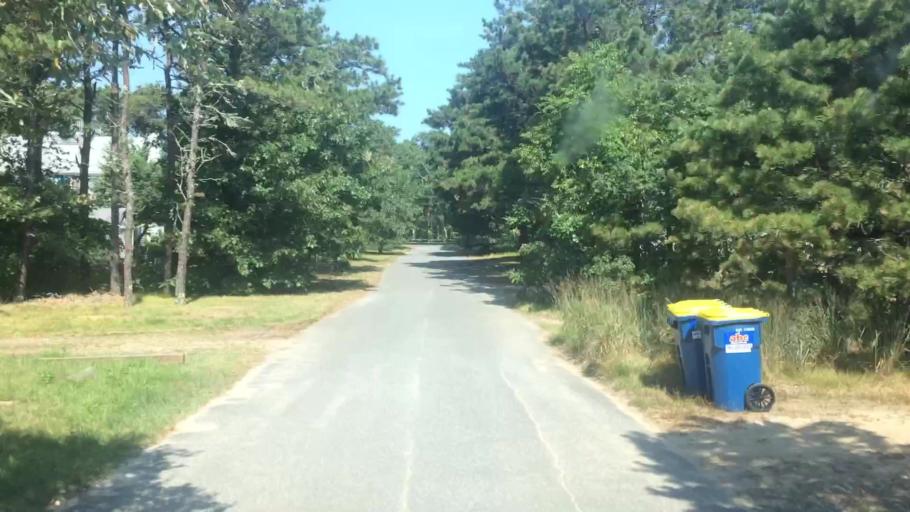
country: US
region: Massachusetts
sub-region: Dukes County
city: Edgartown
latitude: 41.3720
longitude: -70.5319
